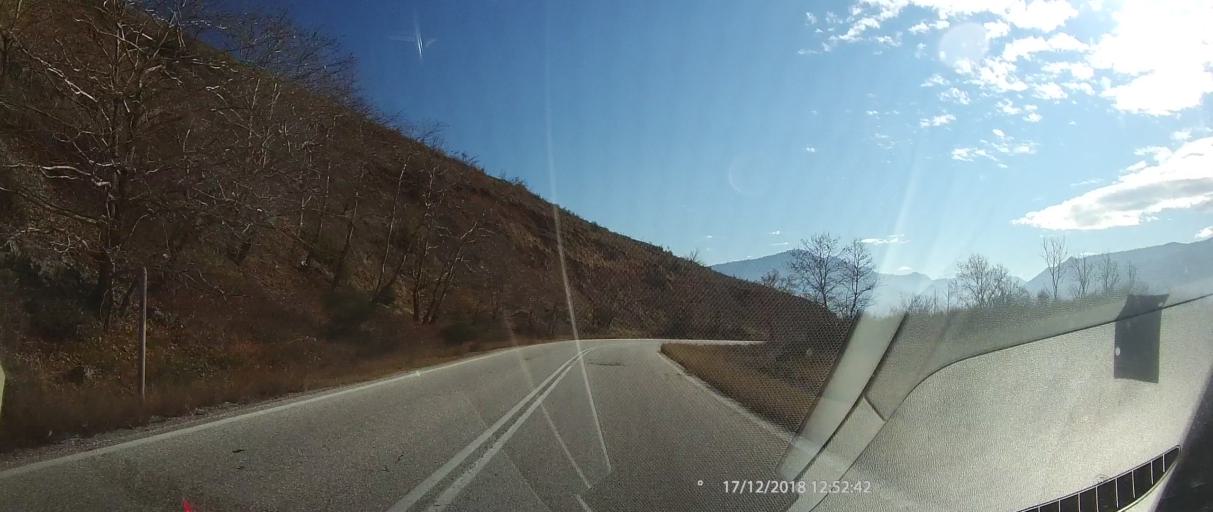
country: GR
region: Thessaly
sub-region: Trikala
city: Kastraki
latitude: 39.7586
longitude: 21.4823
